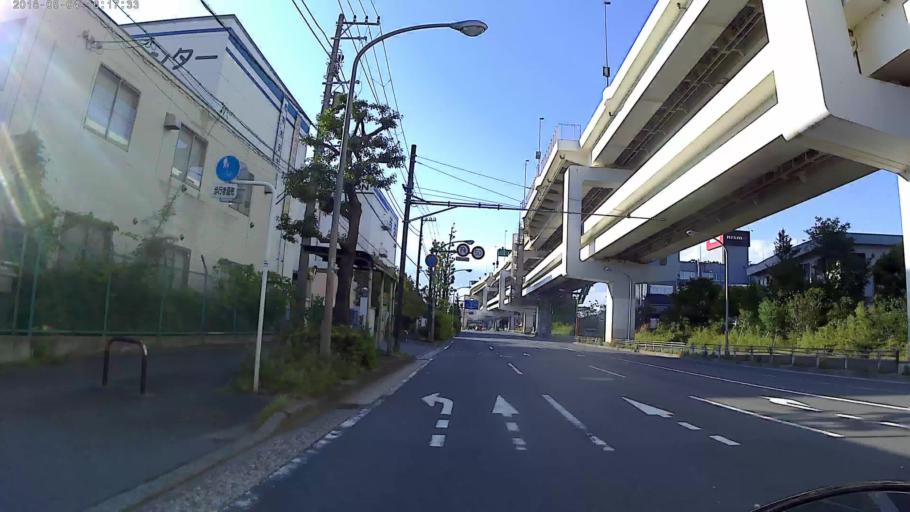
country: JP
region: Kanagawa
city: Yokohama
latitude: 35.4848
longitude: 139.6750
